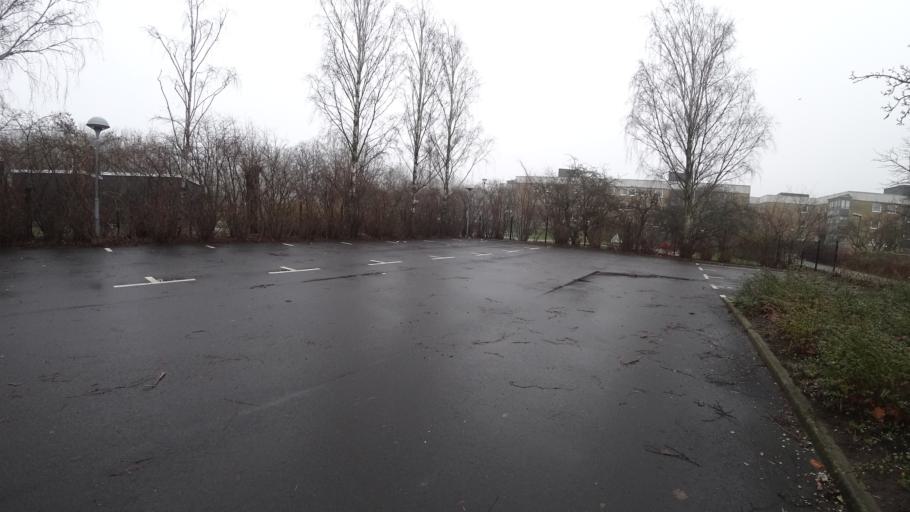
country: SE
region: Skane
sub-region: Malmo
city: Malmoe
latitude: 55.5781
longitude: 12.9918
